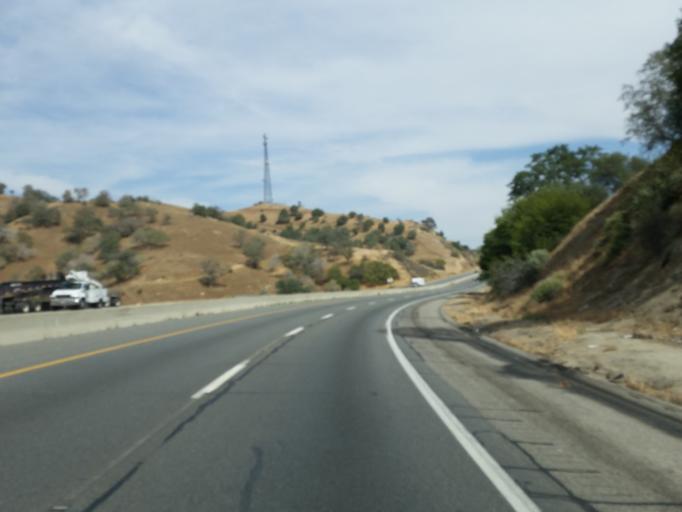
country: US
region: California
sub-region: Kern County
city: Bear Valley Springs
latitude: 35.2557
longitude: -118.6092
